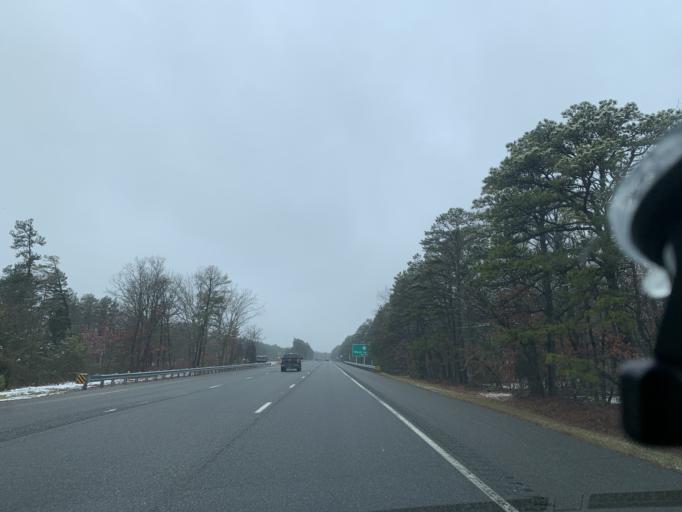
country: US
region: New Jersey
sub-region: Atlantic County
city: Pomona
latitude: 39.4424
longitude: -74.6083
